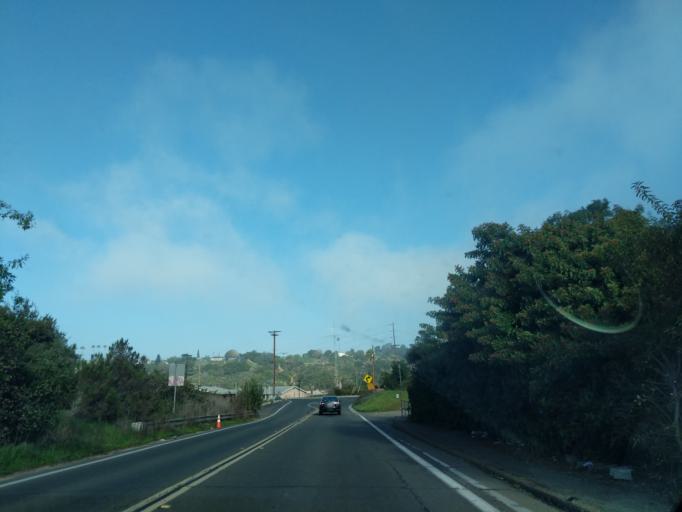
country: US
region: California
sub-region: San Diego County
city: National City
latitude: 32.7283
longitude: -117.0881
